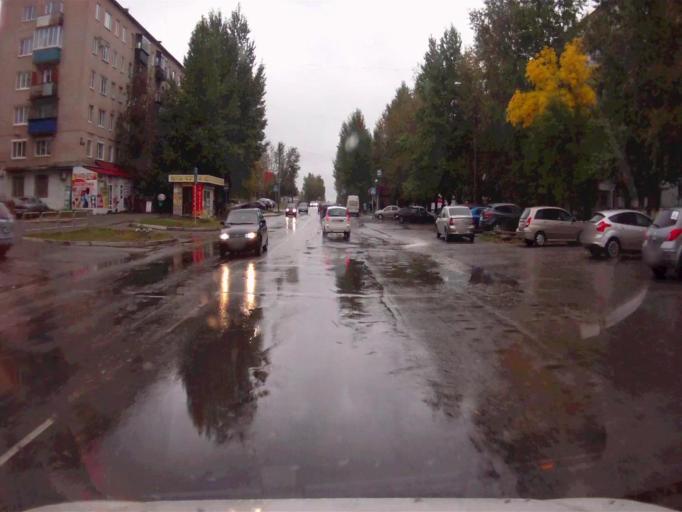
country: RU
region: Chelyabinsk
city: Kyshtym
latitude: 55.7025
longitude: 60.5560
